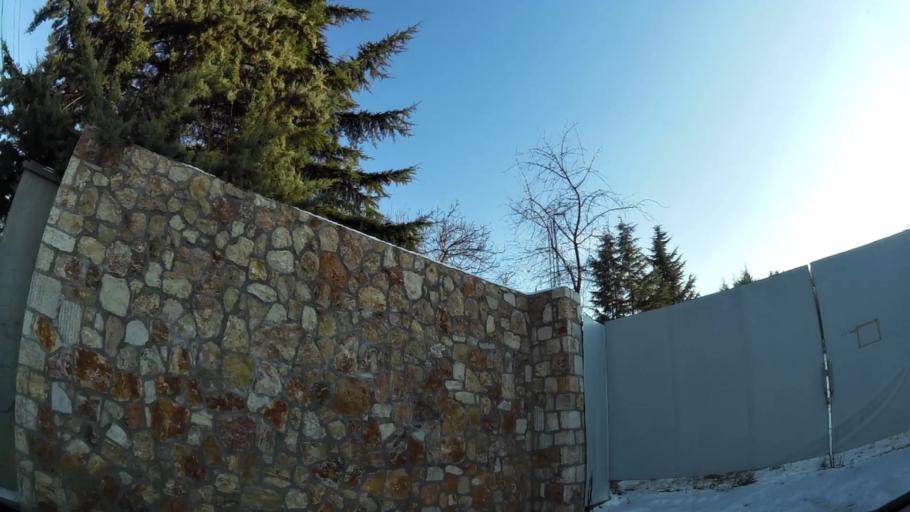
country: MK
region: Karpos
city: Skopje
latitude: 41.9900
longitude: 21.4036
